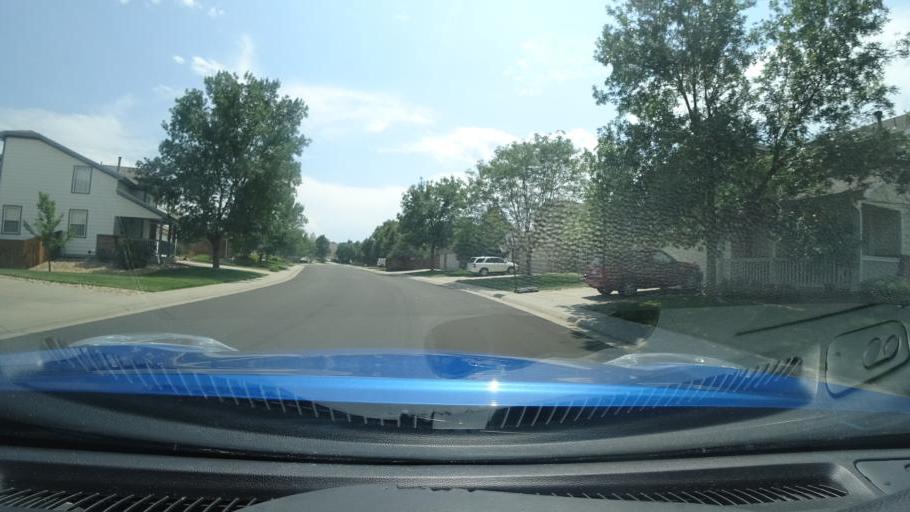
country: US
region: Colorado
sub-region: Adams County
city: Aurora
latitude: 39.6638
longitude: -104.7754
